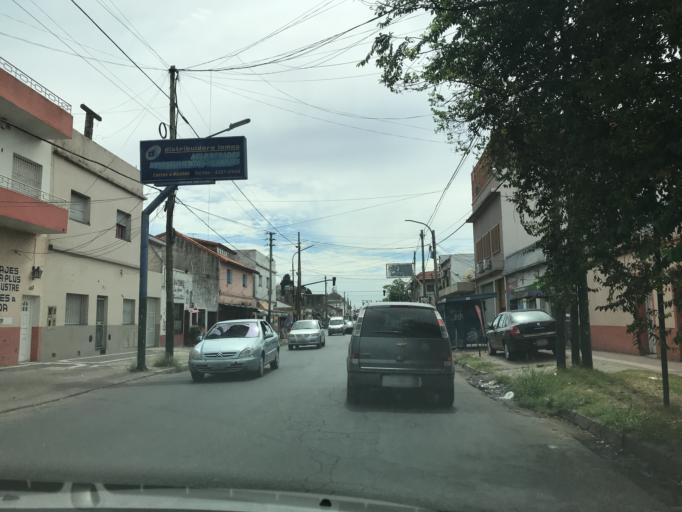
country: AR
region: Buenos Aires
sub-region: Partido de Lomas de Zamora
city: Lomas de Zamora
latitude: -34.7298
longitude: -58.4232
